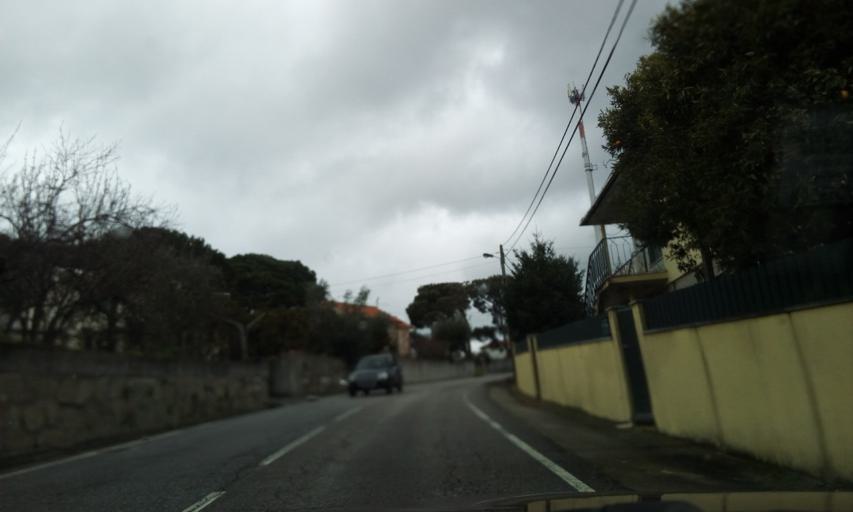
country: PT
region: Viseu
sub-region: Viseu
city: Rio de Loba
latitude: 40.6259
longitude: -7.8673
